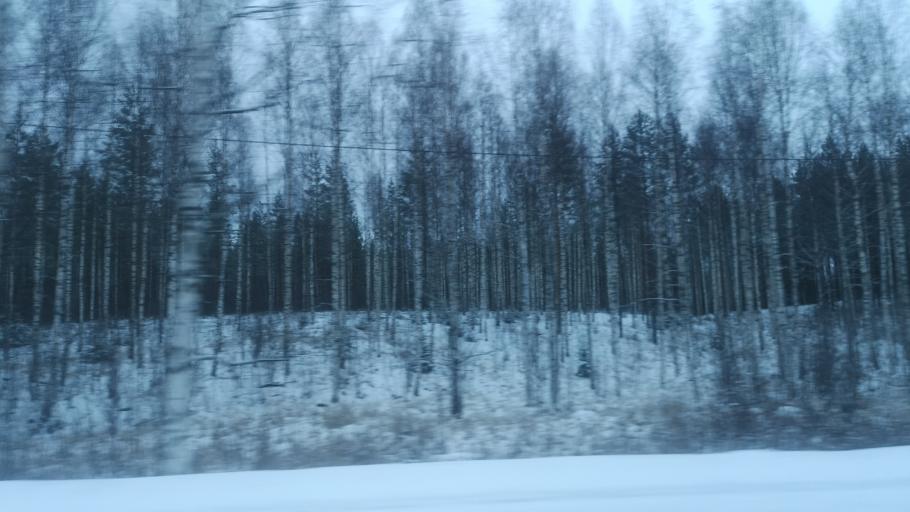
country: FI
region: Southern Savonia
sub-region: Savonlinna
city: Enonkoski
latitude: 62.0960
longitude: 28.6673
